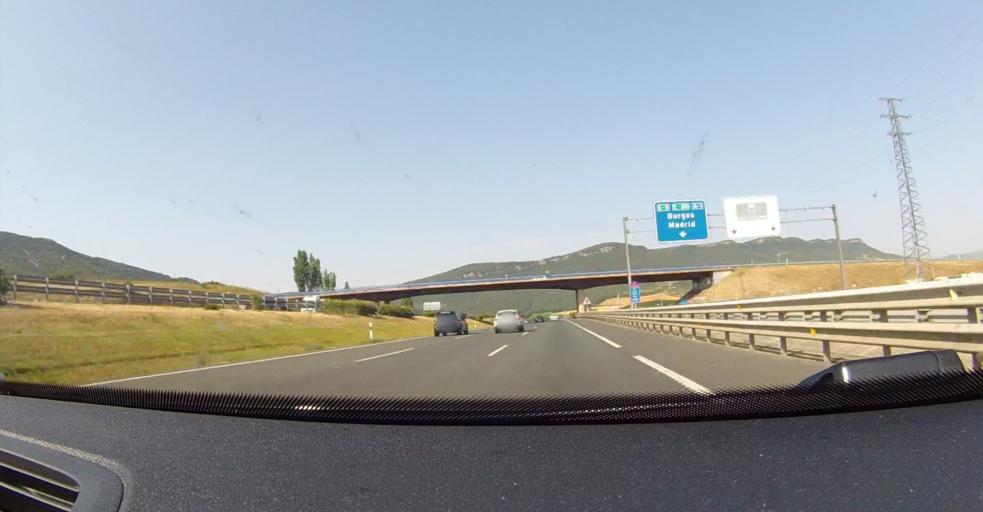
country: ES
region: Basque Country
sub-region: Provincia de Alava
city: Arminon
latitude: 42.8058
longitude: -2.8071
